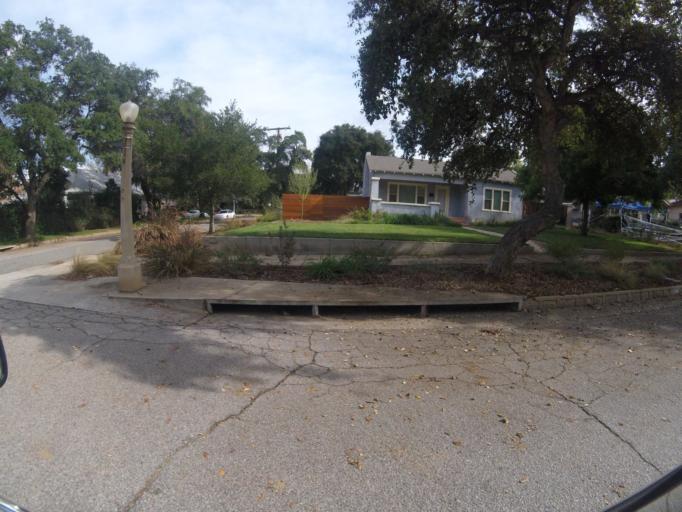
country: US
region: California
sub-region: San Bernardino County
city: Redlands
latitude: 34.0468
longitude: -117.1813
